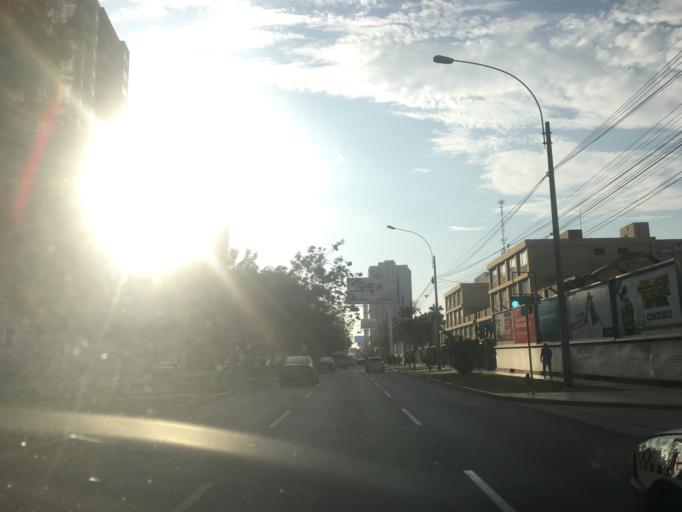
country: PE
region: Lima
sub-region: Lima
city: San Isidro
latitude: -12.0919
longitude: -77.0547
